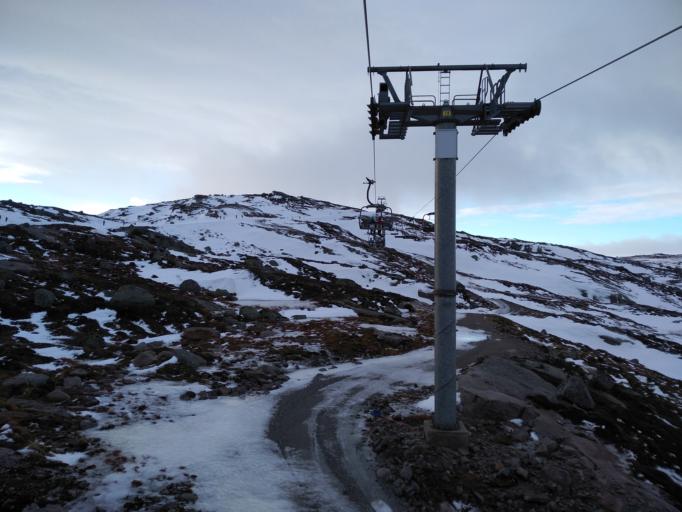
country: NO
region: Vest-Agder
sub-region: Sirdal
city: Tonstad
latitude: 58.9124
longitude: 6.8210
